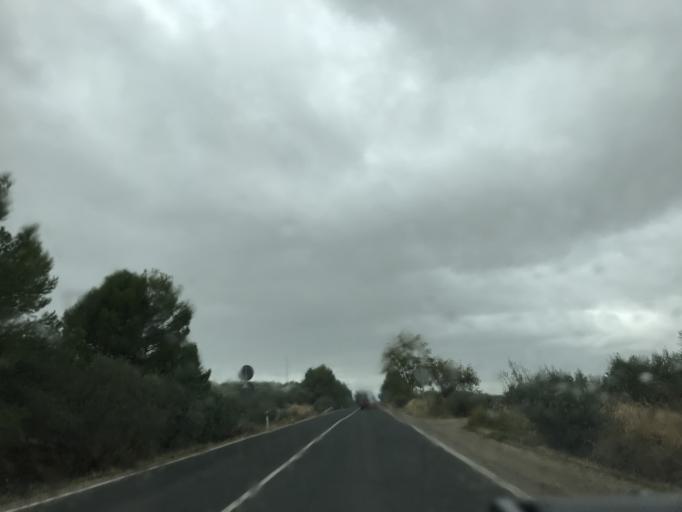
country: ES
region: Andalusia
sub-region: Provincia de Jaen
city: Peal de Becerro
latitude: 37.9185
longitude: -3.1244
